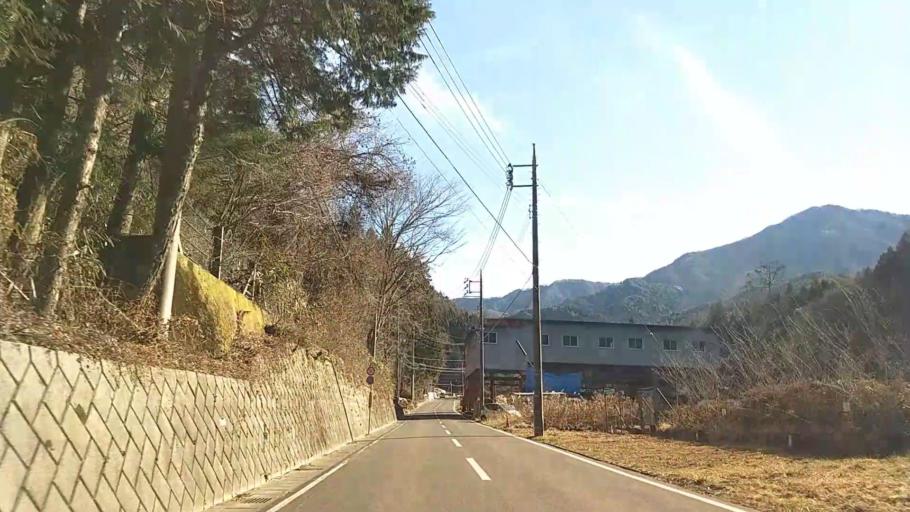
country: JP
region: Yamanashi
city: Otsuki
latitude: 35.5254
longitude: 138.9240
